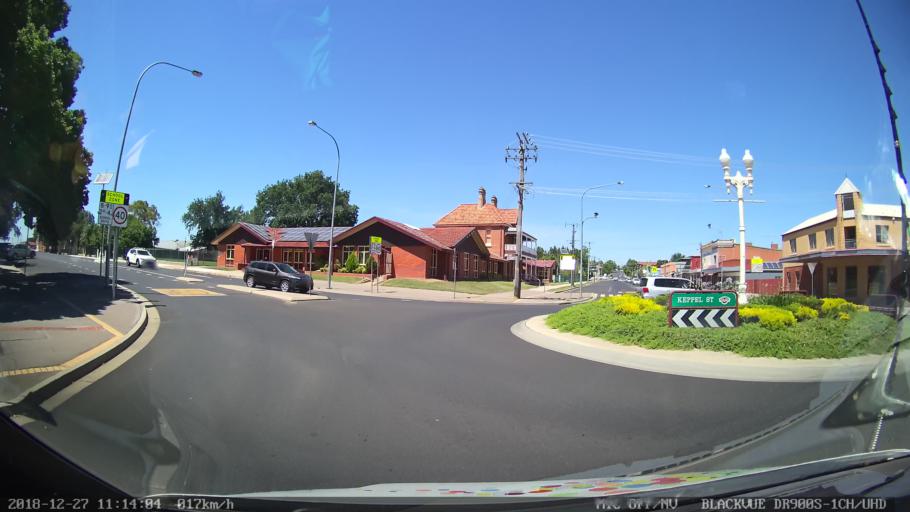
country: AU
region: New South Wales
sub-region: Bathurst Regional
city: Bathurst
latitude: -33.4182
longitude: 149.5766
